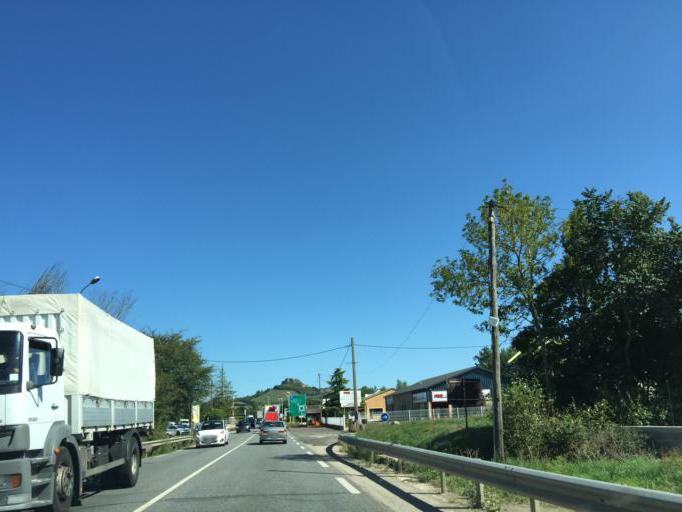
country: FR
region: Midi-Pyrenees
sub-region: Departement de l'Aveyron
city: Severac-le-Chateau
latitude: 44.3327
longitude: 3.0400
